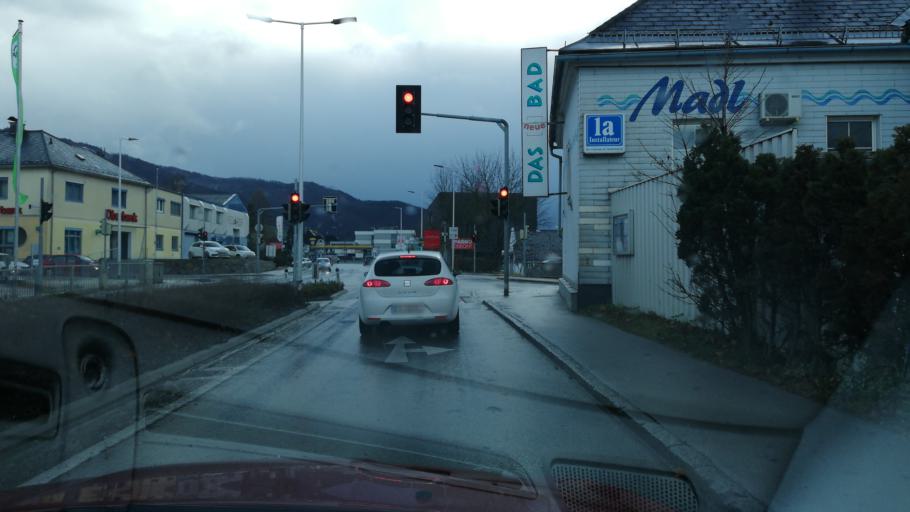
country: AT
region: Upper Austria
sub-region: Politischer Bezirk Kirchdorf an der Krems
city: Micheldorf in Oberoesterreich
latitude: 47.9055
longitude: 14.1201
